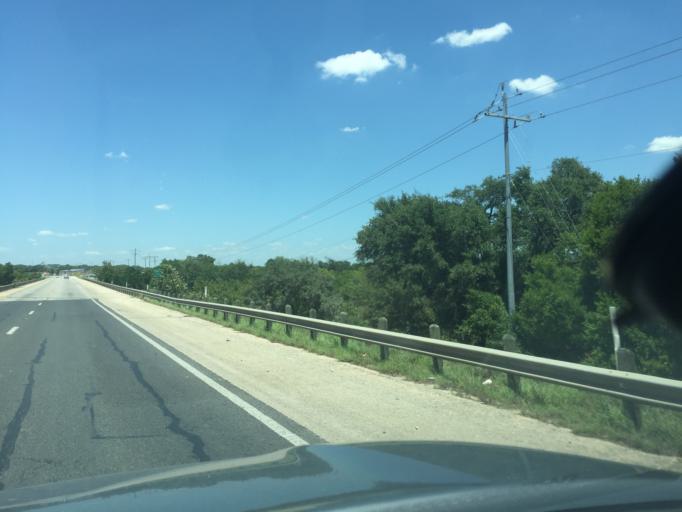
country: US
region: Texas
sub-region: Comal County
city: Bulverde
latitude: 29.7183
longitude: -98.4441
